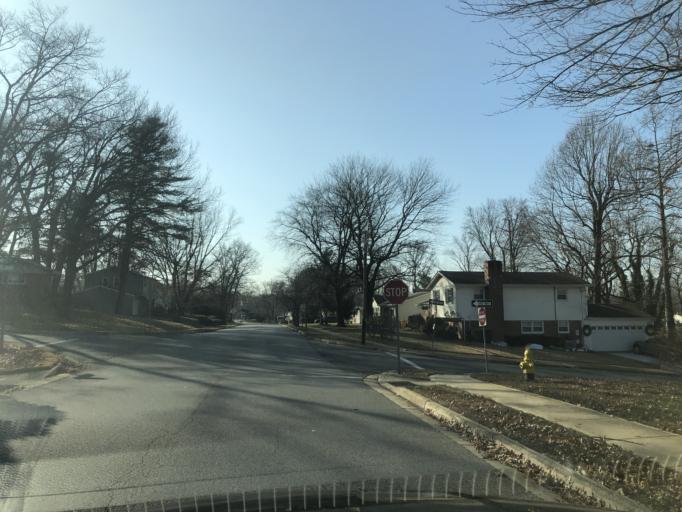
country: US
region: Maryland
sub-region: Anne Arundel County
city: Odenton
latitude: 39.0748
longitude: -76.6937
